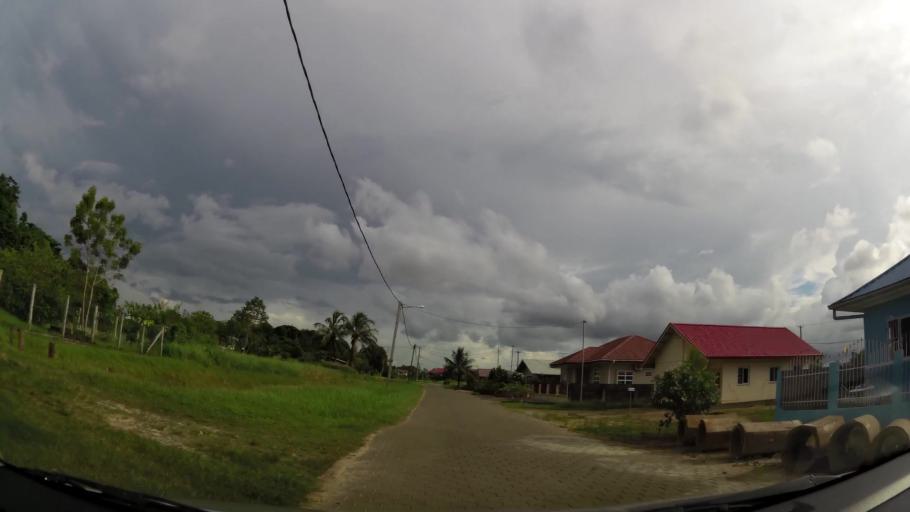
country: SR
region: Paramaribo
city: Paramaribo
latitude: 5.8473
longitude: -55.1773
